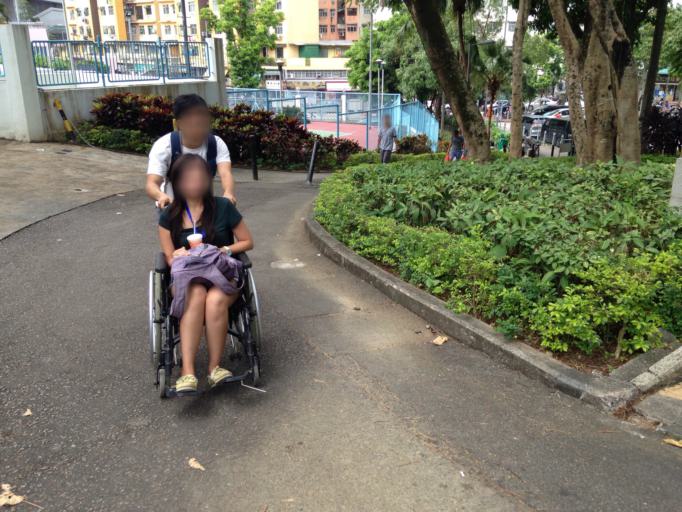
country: HK
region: Tai Po
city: Tai Po
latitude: 22.4463
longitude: 114.1686
